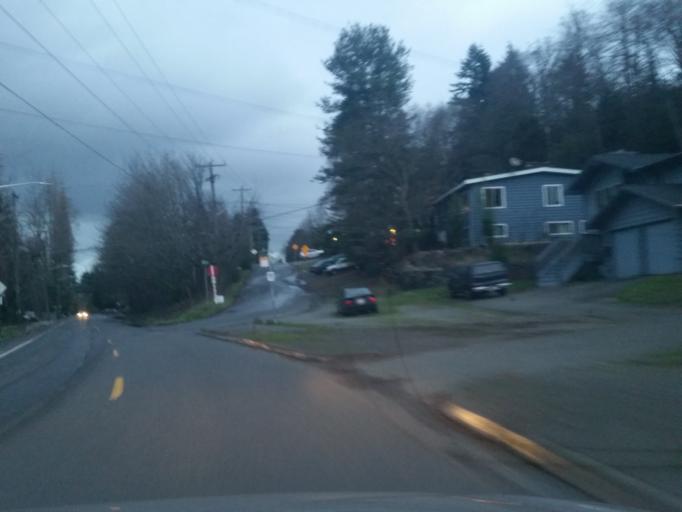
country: US
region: Washington
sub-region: King County
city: Lake Forest Park
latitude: 47.6896
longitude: -122.3015
